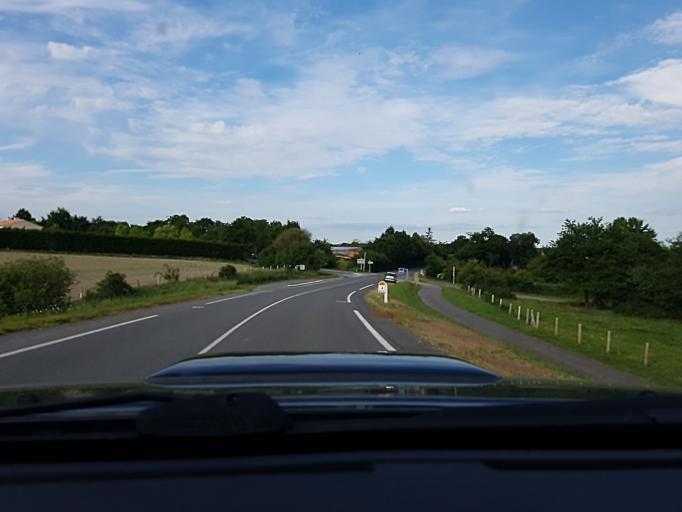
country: FR
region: Pays de la Loire
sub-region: Departement de la Vendee
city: Mache
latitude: 46.7735
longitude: -1.6693
